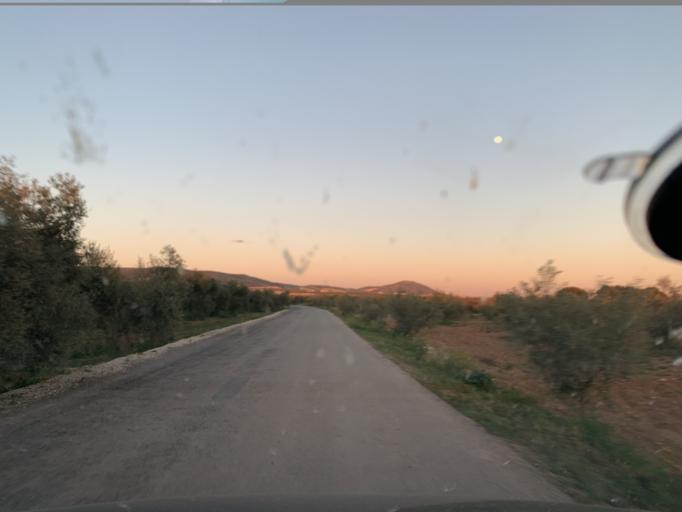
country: ES
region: Andalusia
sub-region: Provincia de Sevilla
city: Gilena
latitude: 37.2274
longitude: -4.9308
